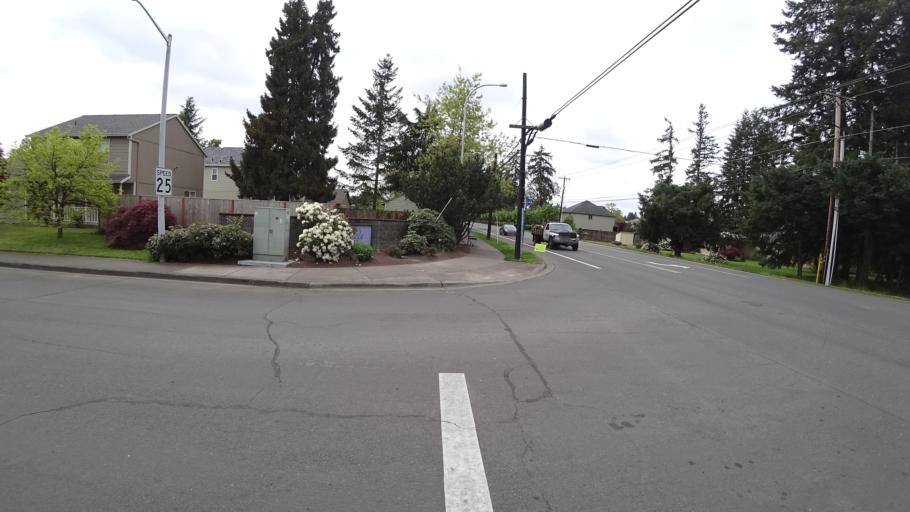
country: US
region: Oregon
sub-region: Washington County
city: Hillsboro
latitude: 45.5487
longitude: -122.9954
